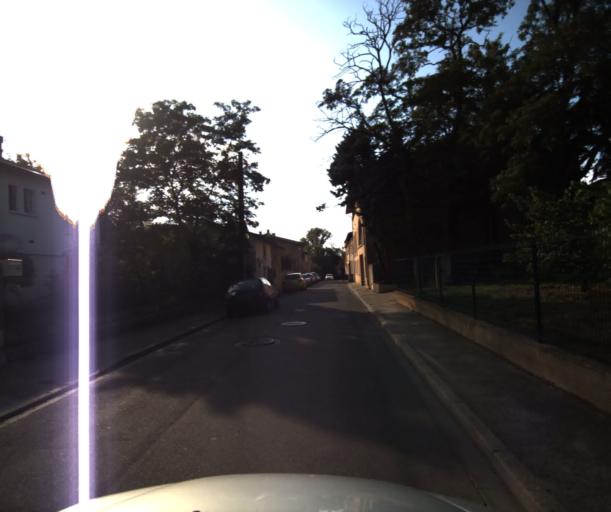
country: FR
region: Midi-Pyrenees
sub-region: Departement de la Haute-Garonne
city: Muret
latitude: 43.4575
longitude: 1.3304
